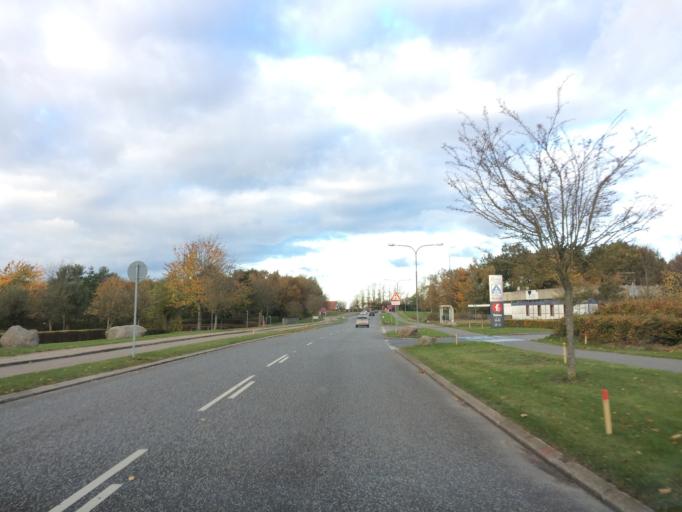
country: DK
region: South Denmark
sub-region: Sonderborg Kommune
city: Nordborg
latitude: 55.0406
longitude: 9.7908
